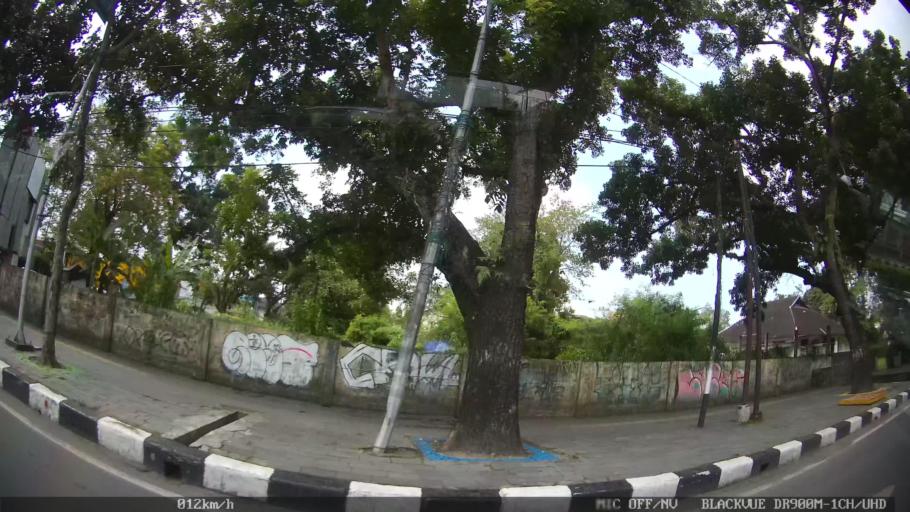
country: ID
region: North Sumatra
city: Medan
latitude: 3.5773
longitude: 98.6670
